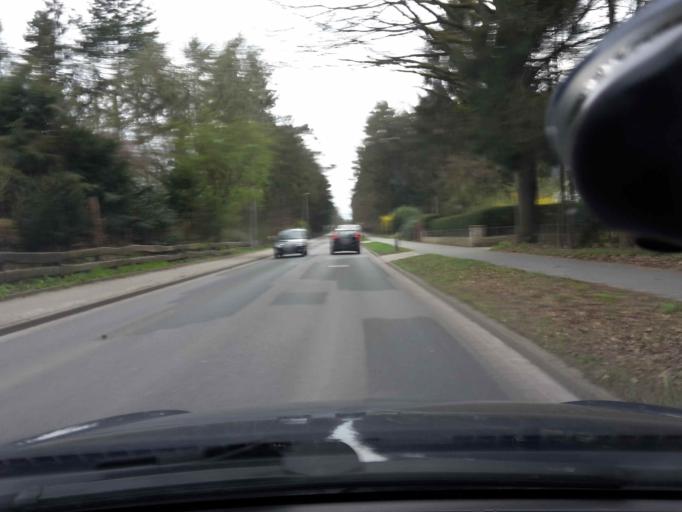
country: DE
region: Lower Saxony
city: Buchholz in der Nordheide
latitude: 53.2944
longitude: 9.8700
